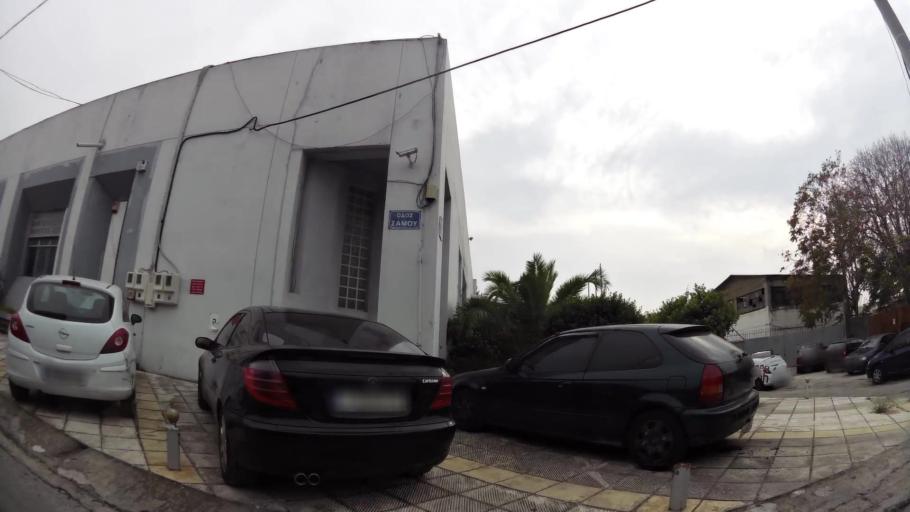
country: GR
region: Attica
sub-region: Nomarchia Athinas
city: Tavros
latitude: 37.9733
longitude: 23.6984
